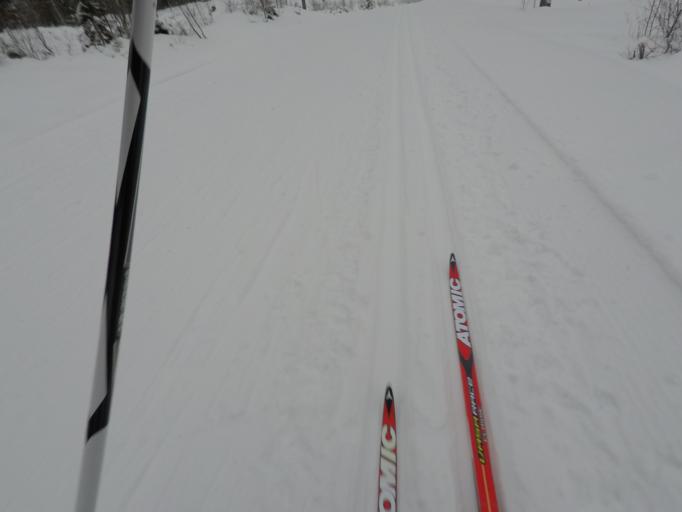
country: SE
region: Dalarna
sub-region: Ludvika Kommun
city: Abborrberget
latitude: 60.1492
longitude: 14.4893
